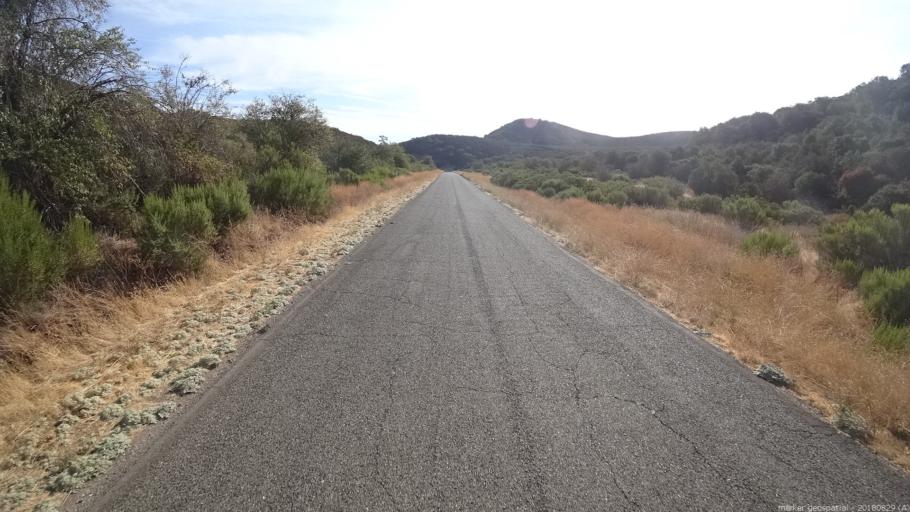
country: US
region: California
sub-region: Monterey County
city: King City
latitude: 36.0457
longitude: -121.0637
